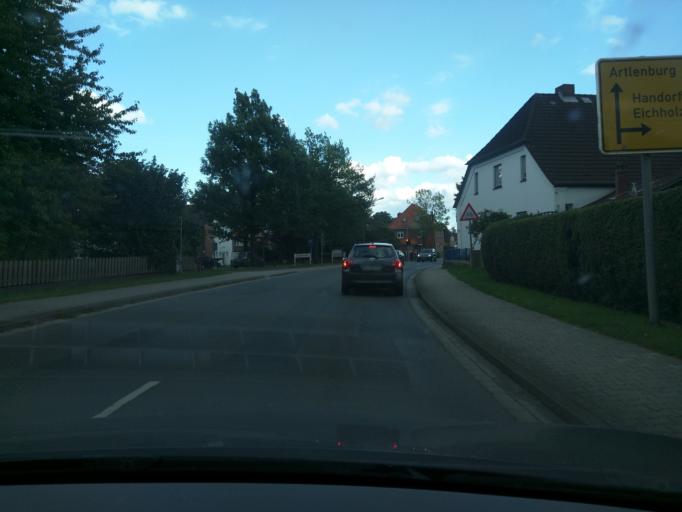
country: DE
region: Lower Saxony
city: Marschacht
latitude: 53.4177
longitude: 10.3667
